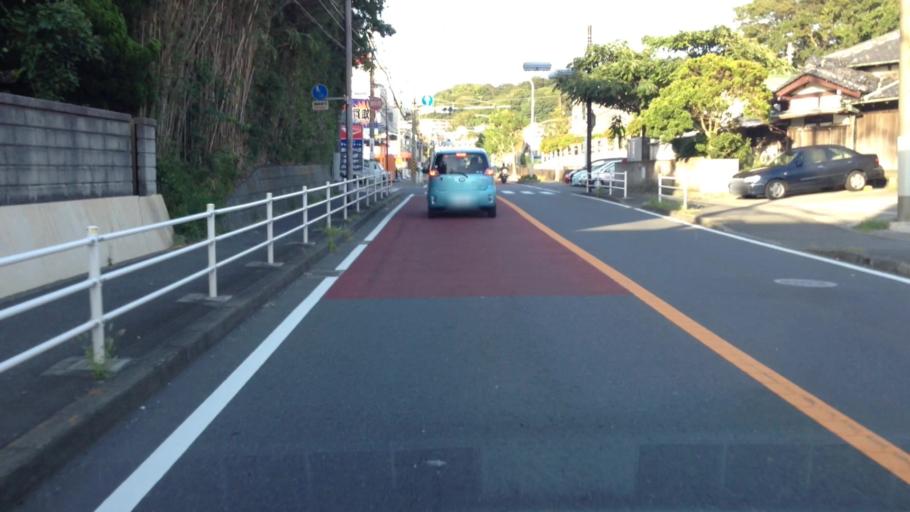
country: JP
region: Kanagawa
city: Yokosuka
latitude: 35.2252
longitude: 139.6456
